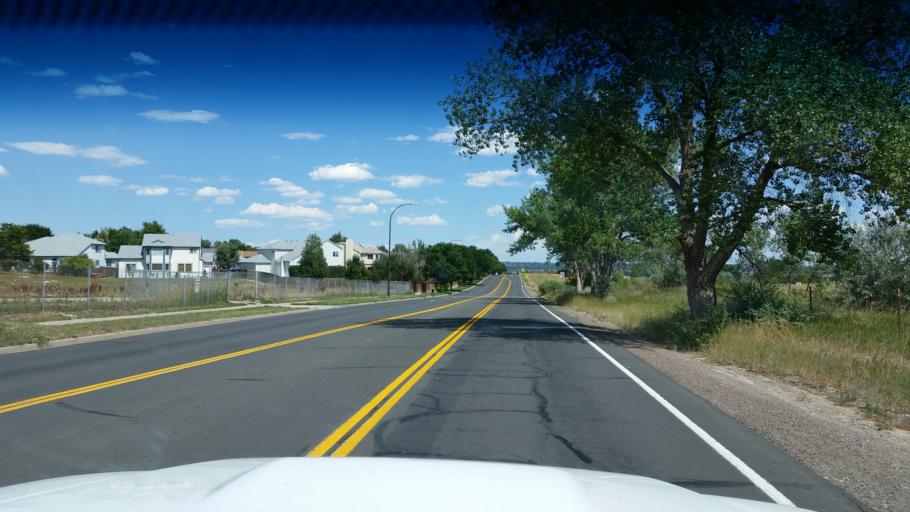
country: US
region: Colorado
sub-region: Broomfield County
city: Broomfield
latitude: 39.8782
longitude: -105.1265
